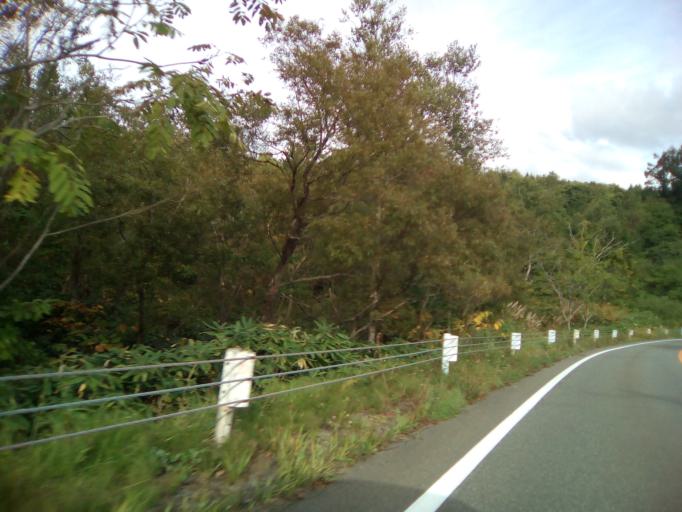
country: JP
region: Hokkaido
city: Date
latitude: 42.6591
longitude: 140.8269
